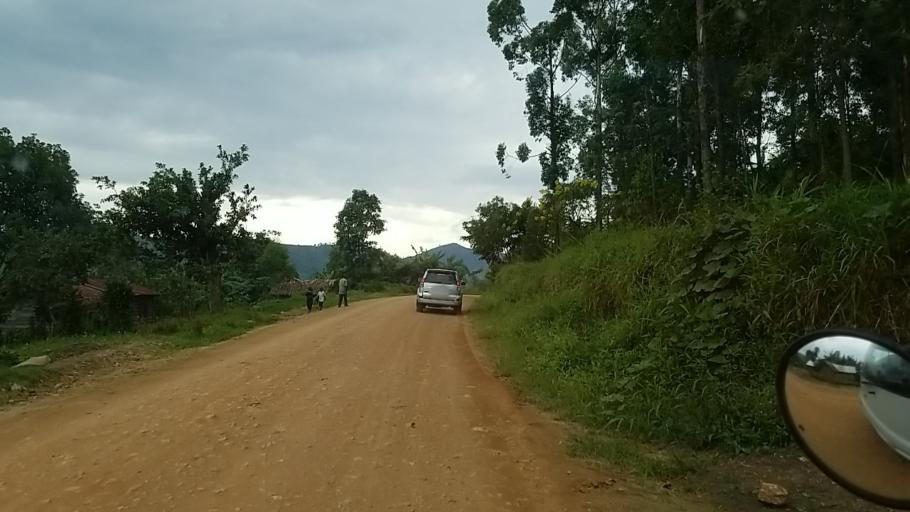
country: CD
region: Nord Kivu
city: Sake
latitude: -1.6730
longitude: 29.0181
